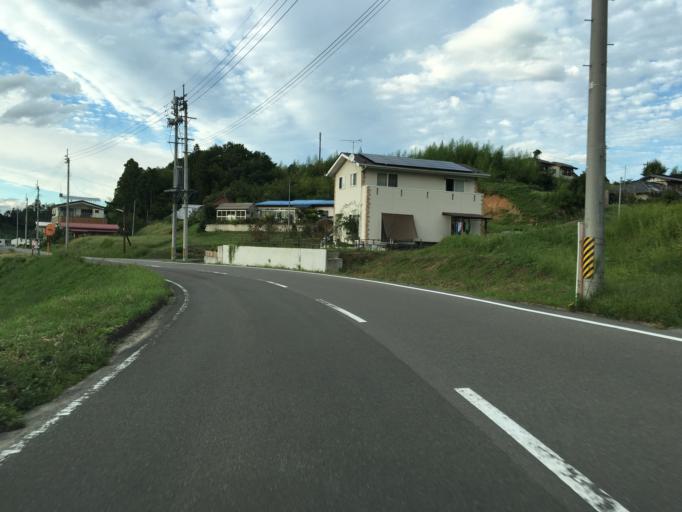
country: JP
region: Fukushima
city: Nihommatsu
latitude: 37.6135
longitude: 140.4958
